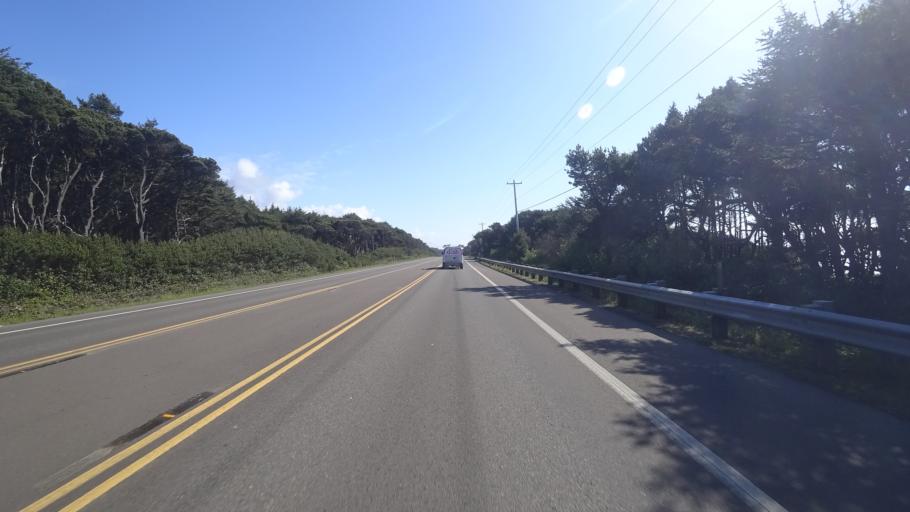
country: US
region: Oregon
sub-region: Lincoln County
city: Newport
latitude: 44.5476
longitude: -124.0729
